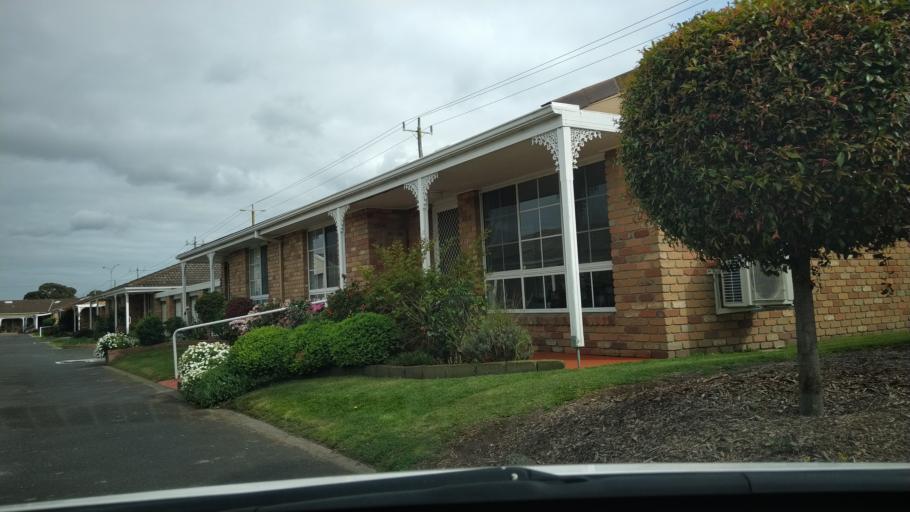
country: AU
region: Victoria
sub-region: Greater Dandenong
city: Keysborough
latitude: -37.9936
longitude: 145.1647
